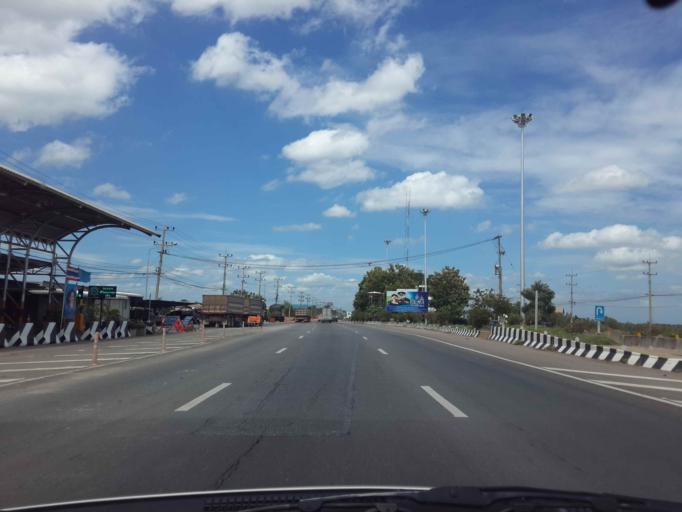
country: TH
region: Samut Songkhram
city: Samut Songkhram
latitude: 13.4489
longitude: 100.0784
